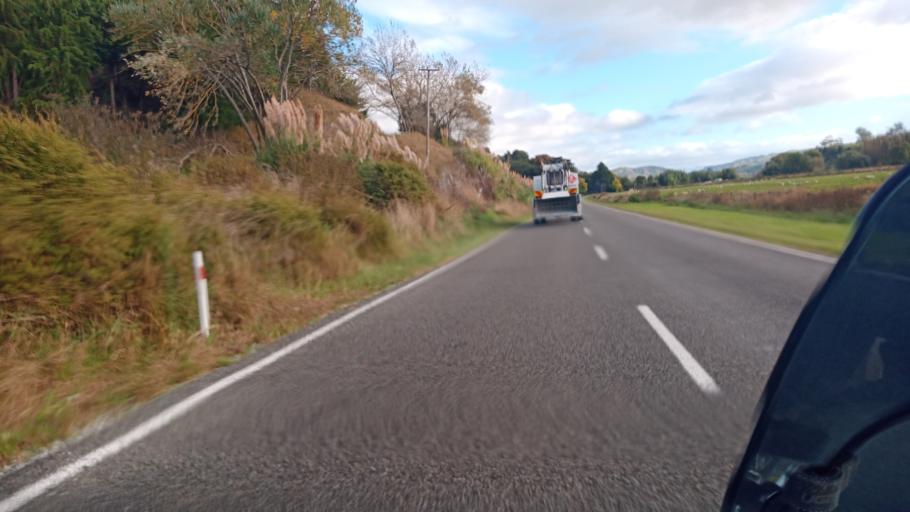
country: NZ
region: Gisborne
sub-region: Gisborne District
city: Gisborne
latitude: -38.6022
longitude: 177.8050
